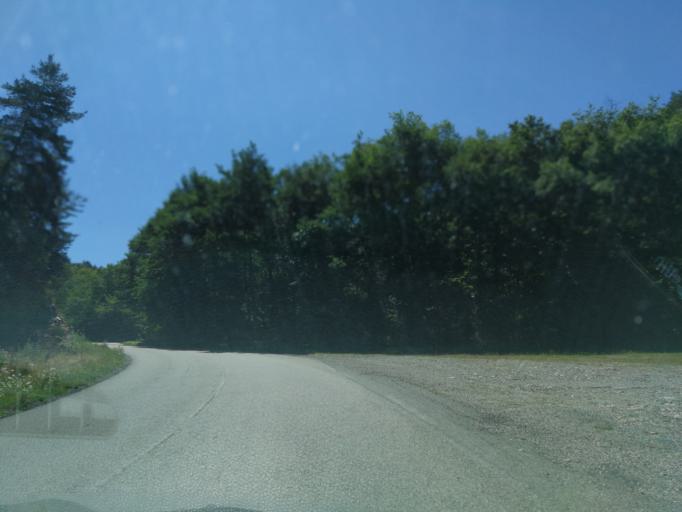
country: FR
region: Limousin
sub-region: Departement de la Correze
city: Argentat
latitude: 45.0588
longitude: 1.9454
